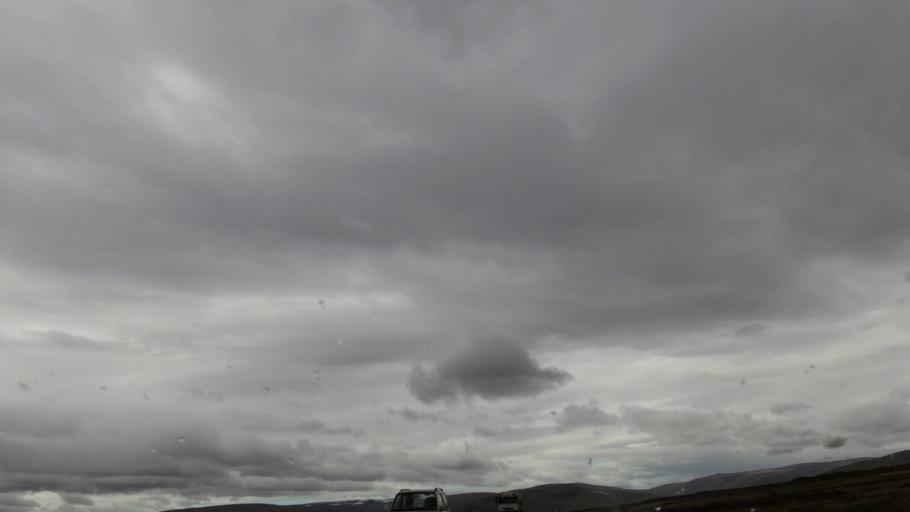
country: IS
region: West
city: Borgarnes
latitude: 65.1753
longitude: -21.7112
